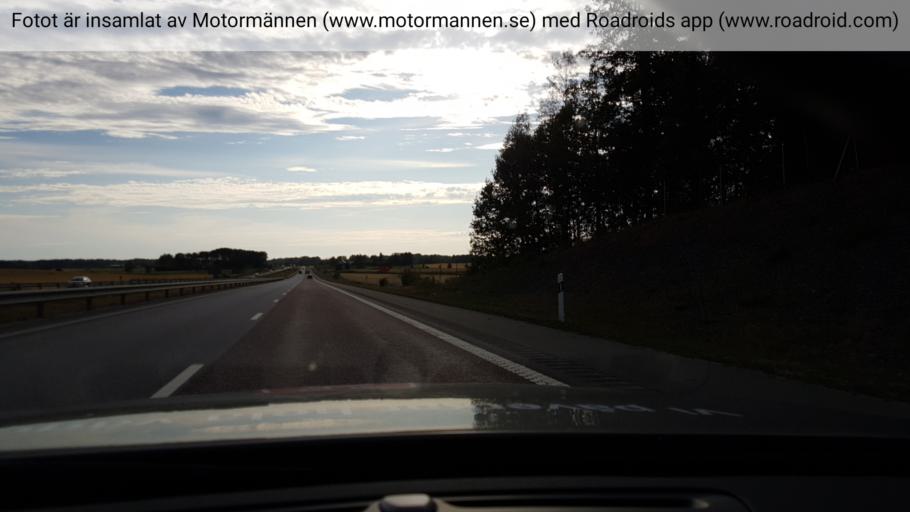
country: SE
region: OErebro
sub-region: Lindesbergs Kommun
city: Frovi
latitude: 59.3084
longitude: 15.3956
